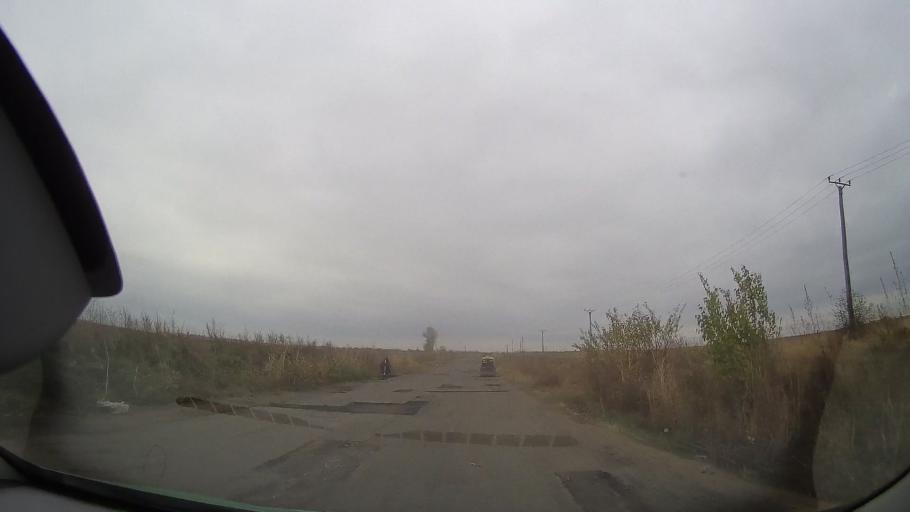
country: RO
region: Braila
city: Dudesti
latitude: 44.9308
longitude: 27.4273
